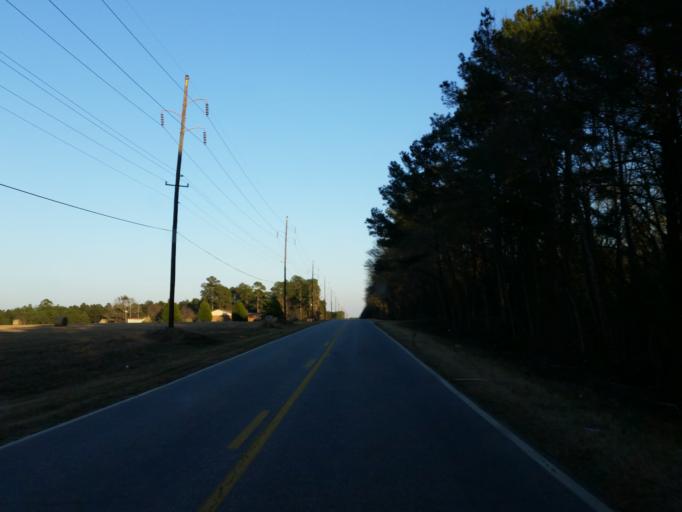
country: US
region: Georgia
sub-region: Crisp County
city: Cordele
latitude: 32.0042
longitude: -83.7783
